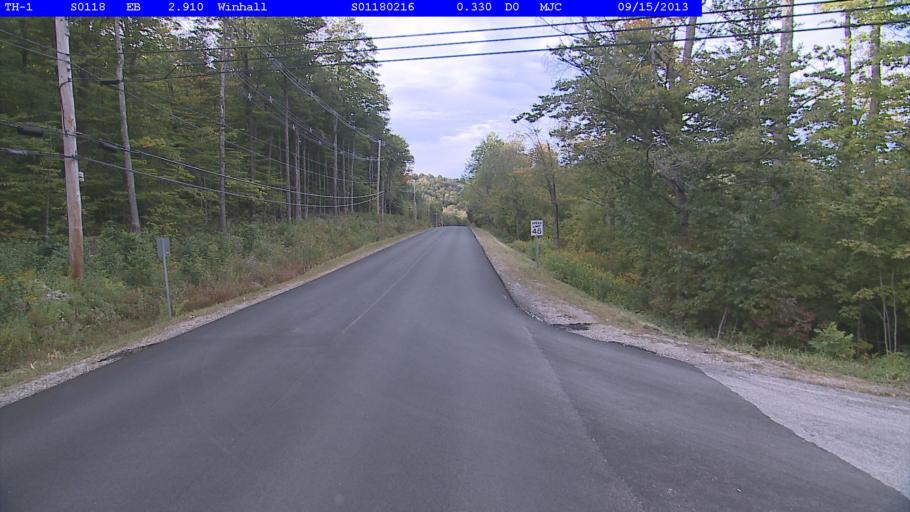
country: US
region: Vermont
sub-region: Bennington County
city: Manchester Center
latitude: 43.1199
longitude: -72.9115
